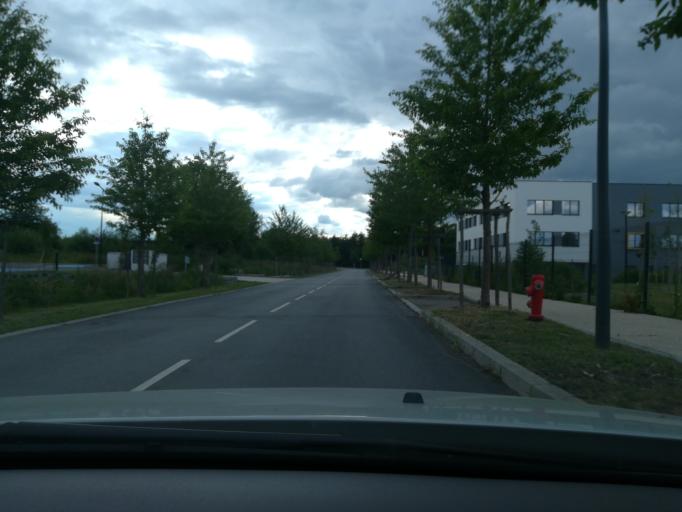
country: FR
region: Haute-Normandie
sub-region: Departement de la Seine-Maritime
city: Isneauville
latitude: 49.4892
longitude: 1.1375
